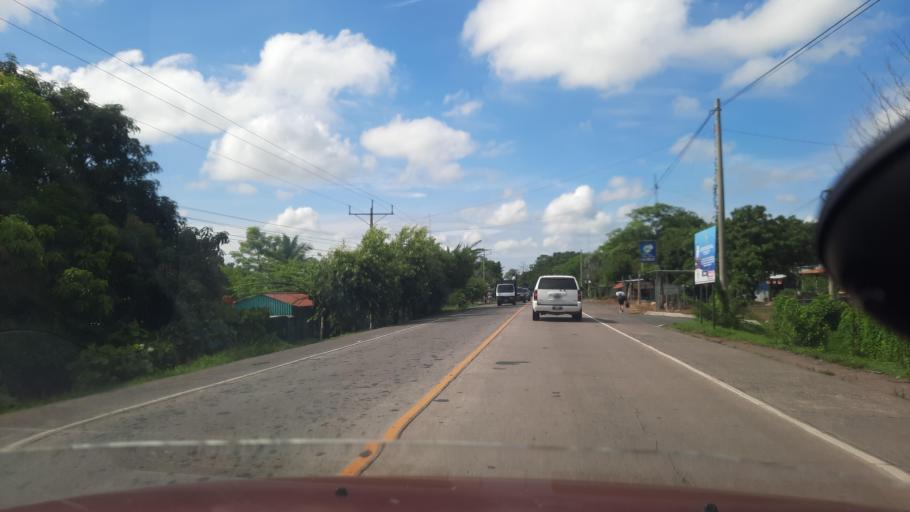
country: SV
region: Usulutan
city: San Agustin
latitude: 13.4322
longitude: -88.7056
